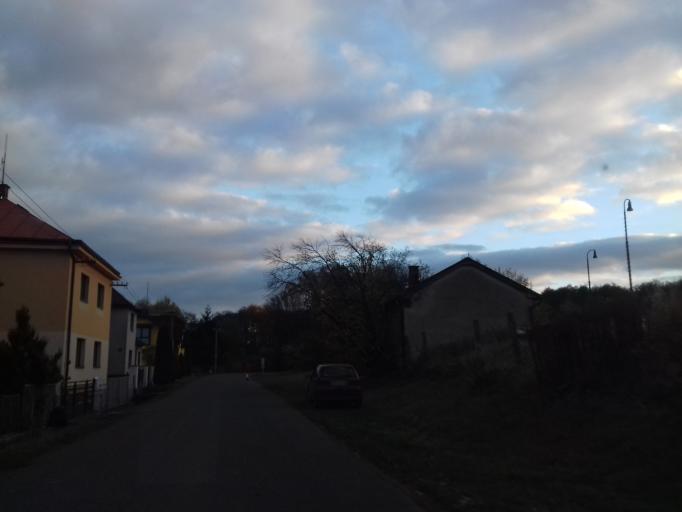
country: CZ
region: Pardubicky
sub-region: Okres Chrudim
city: Skutec
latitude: 49.8254
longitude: 15.9796
